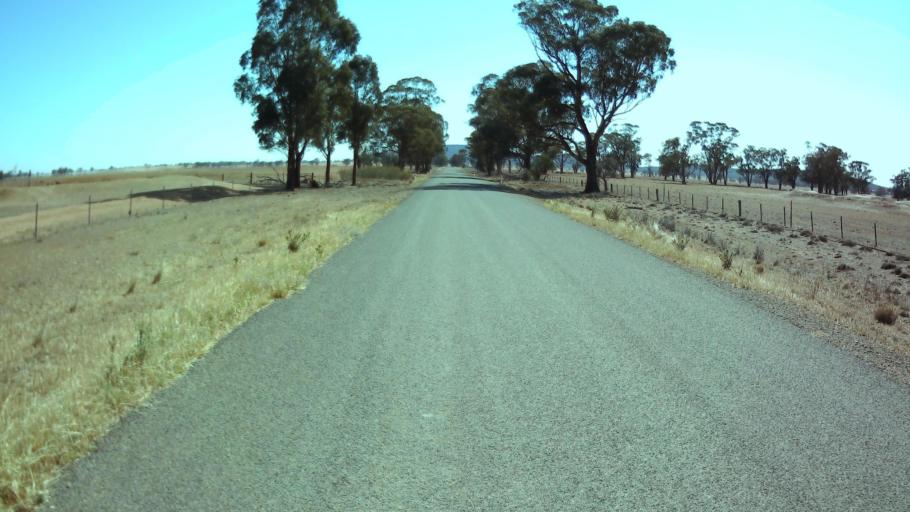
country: AU
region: New South Wales
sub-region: Weddin
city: Grenfell
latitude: -33.7160
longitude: 147.9054
